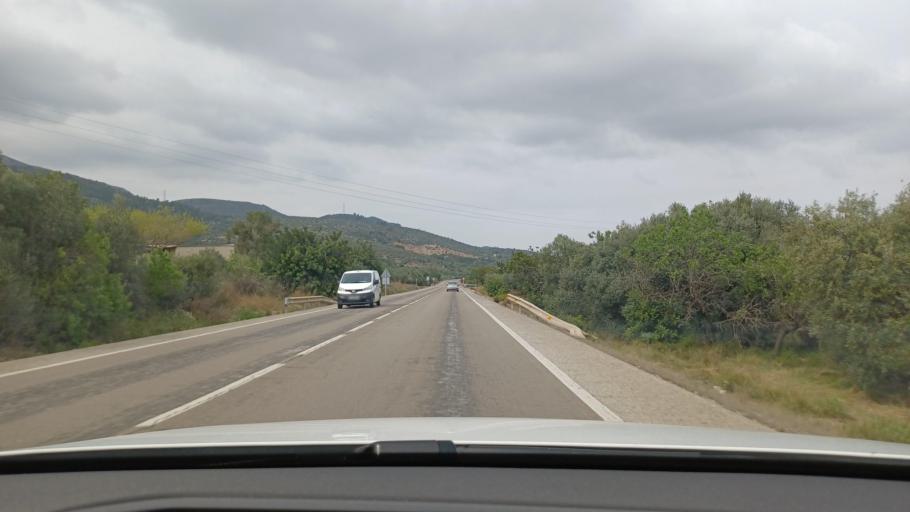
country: ES
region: Catalonia
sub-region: Provincia de Tarragona
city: Sant Carles de la Rapita
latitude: 40.6090
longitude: 0.5693
